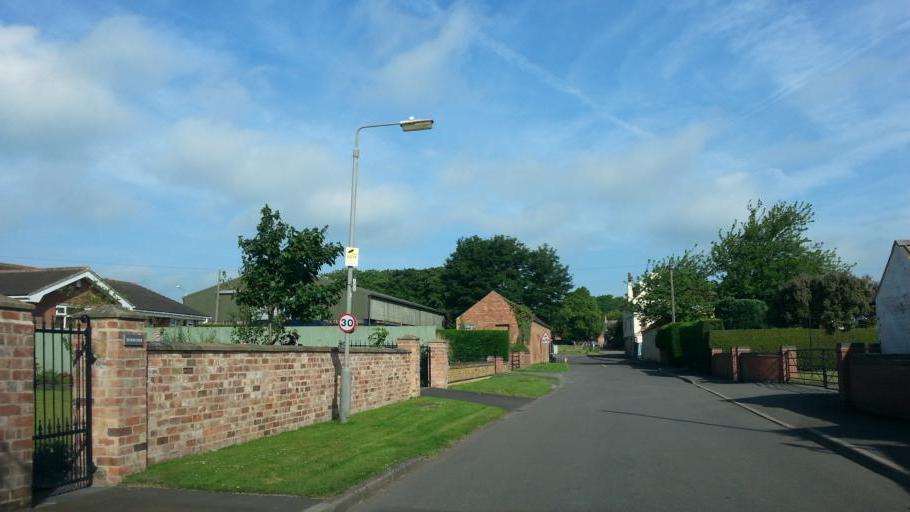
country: GB
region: England
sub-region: Nottinghamshire
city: Farndon
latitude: 53.0384
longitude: -0.8759
